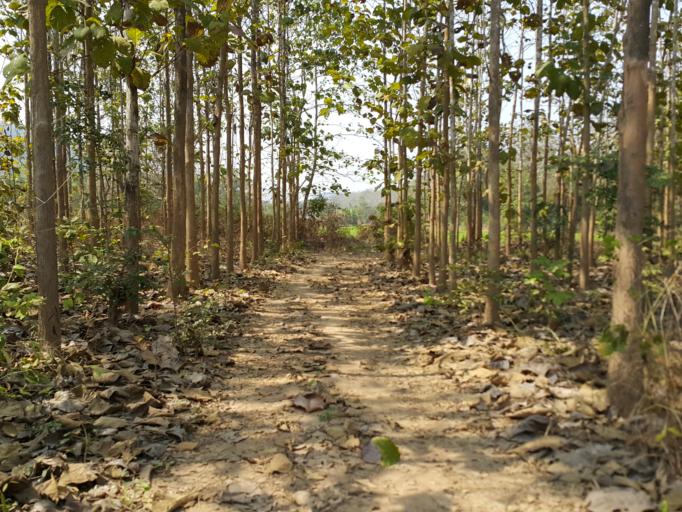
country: TH
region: Sukhothai
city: Thung Saliam
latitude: 17.3288
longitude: 99.4919
